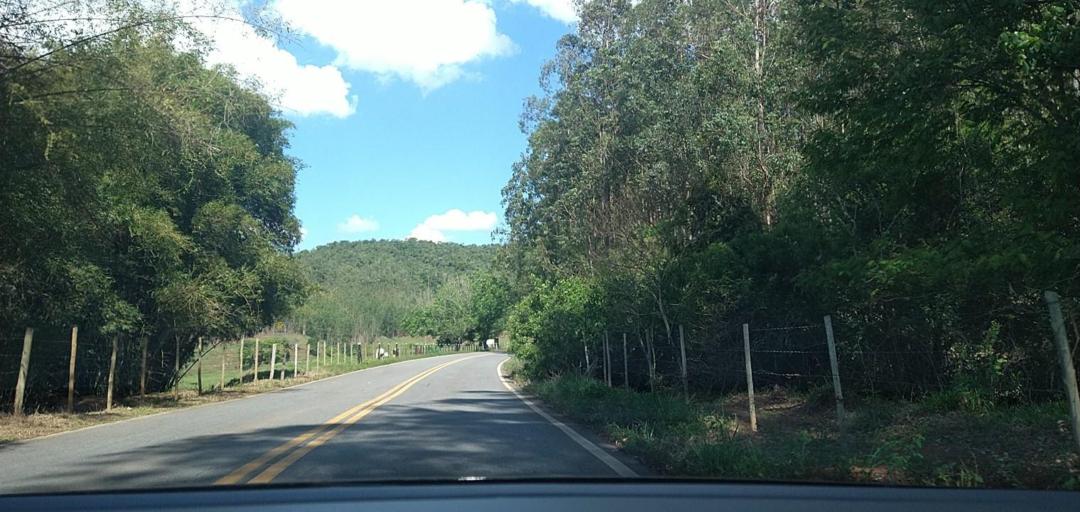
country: BR
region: Minas Gerais
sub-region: Rio Piracicaba
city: Rio Piracicaba
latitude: -19.9803
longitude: -43.1266
